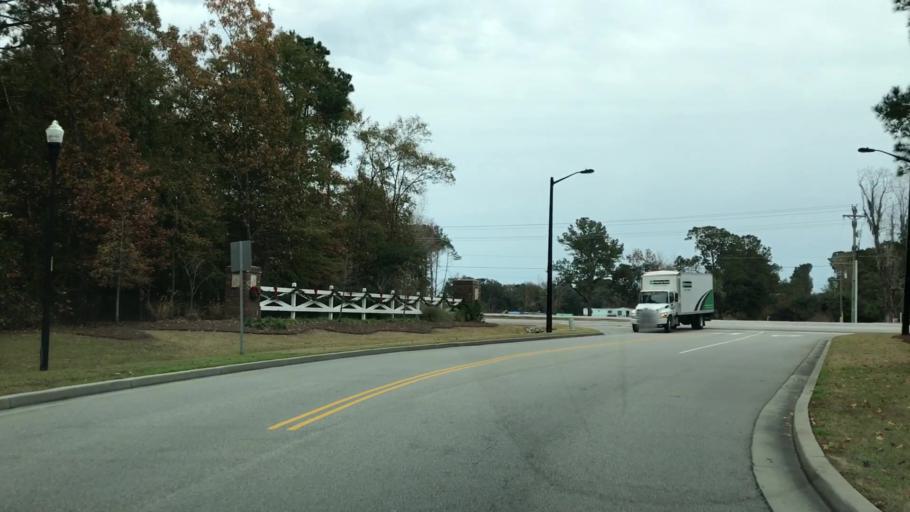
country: US
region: South Carolina
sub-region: Charleston County
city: Isle of Palms
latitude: 32.8880
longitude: -79.7446
